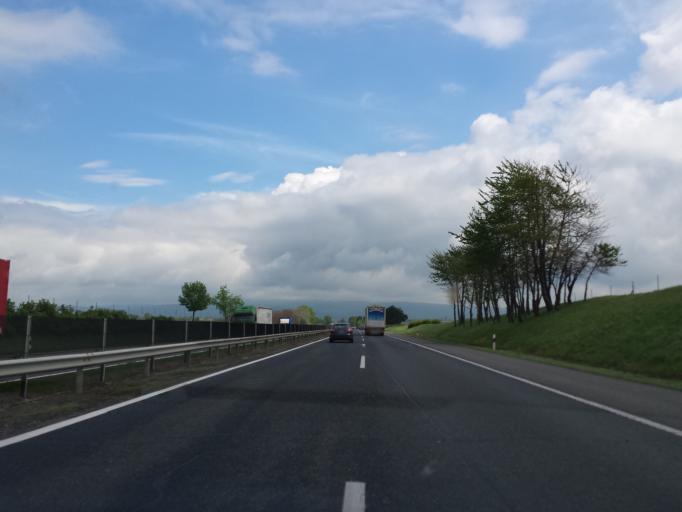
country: HU
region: Komarom-Esztergom
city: Tata
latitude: 47.6253
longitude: 18.2823
